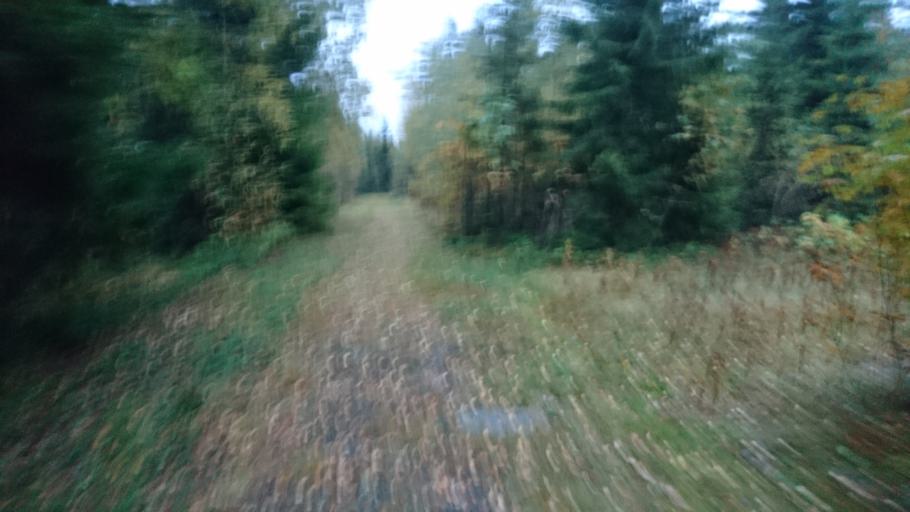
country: SE
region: Vaesterbotten
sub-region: Robertsfors Kommun
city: Robertsfors
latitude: 64.2313
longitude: 20.9941
